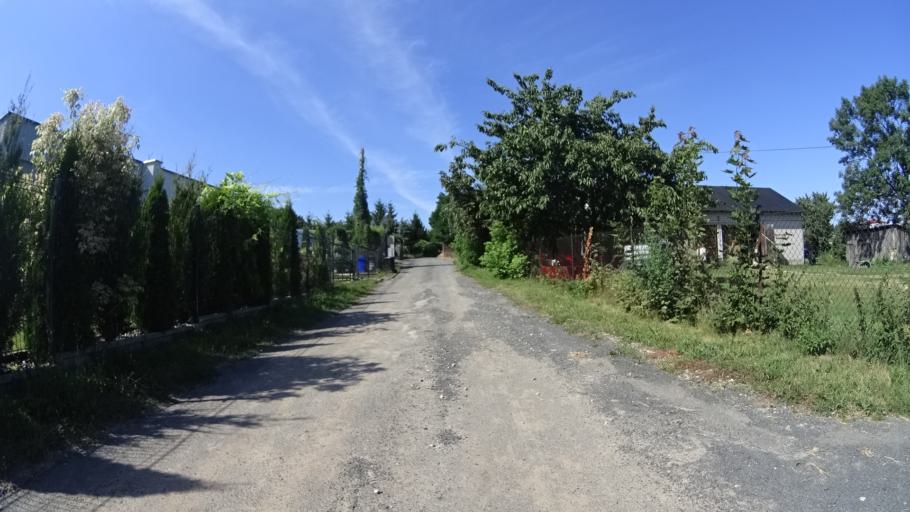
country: PL
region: Masovian Voivodeship
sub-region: Powiat bialobrzeski
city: Promna
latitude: 51.6690
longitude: 20.9353
